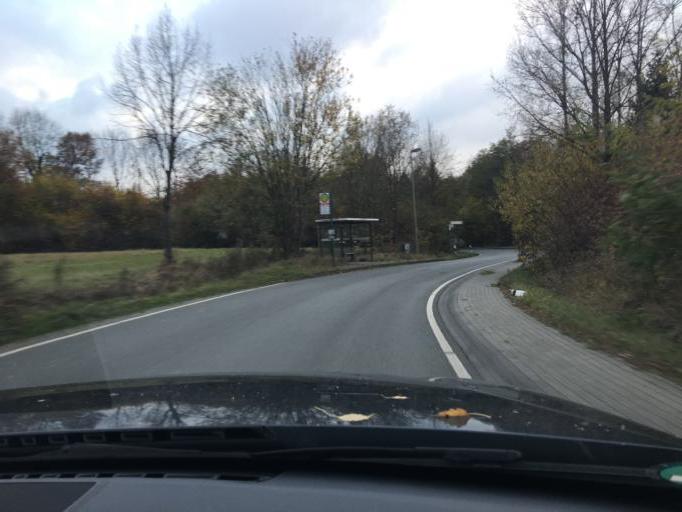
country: DE
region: North Rhine-Westphalia
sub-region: Regierungsbezirk Munster
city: Muenster
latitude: 51.9971
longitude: 7.6908
